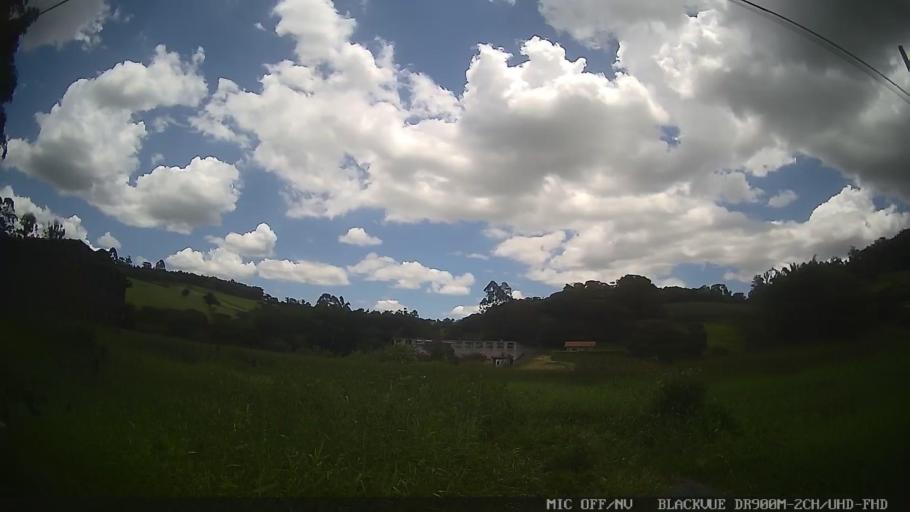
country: BR
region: Sao Paulo
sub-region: Braganca Paulista
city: Braganca Paulista
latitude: -23.0108
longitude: -46.4907
